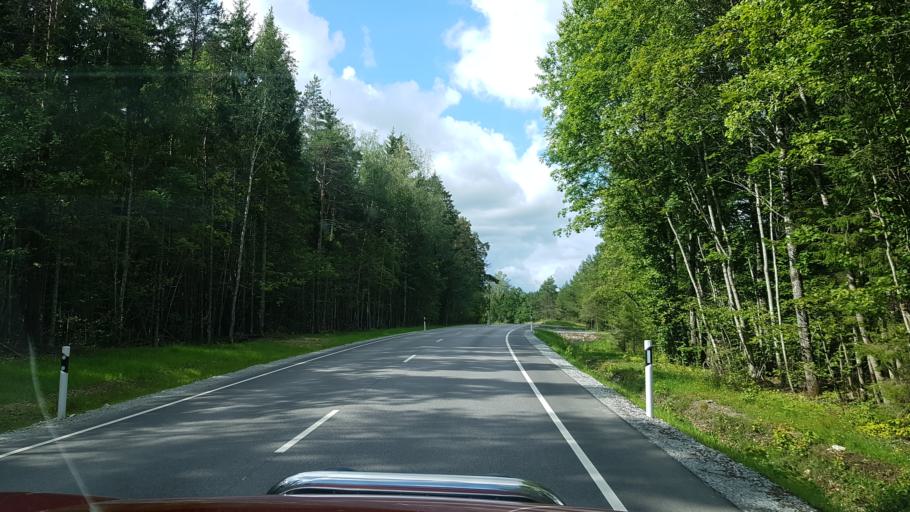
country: EE
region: Harju
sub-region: Keila linn
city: Keila
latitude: 59.1952
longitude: 24.4023
